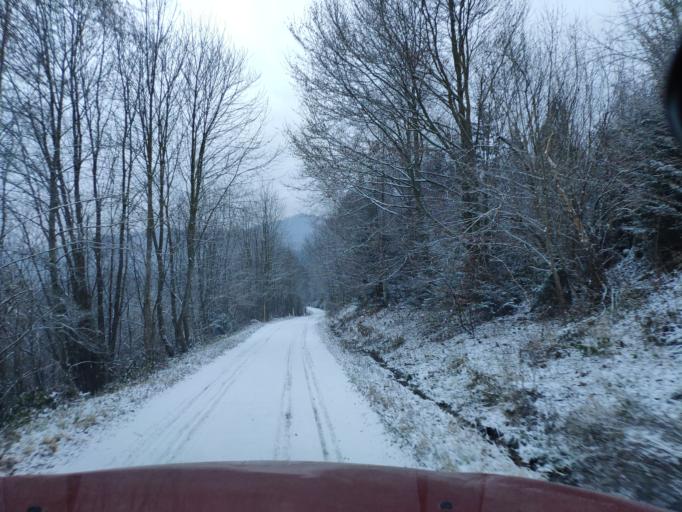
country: SK
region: Kosicky
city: Spisska Nova Ves
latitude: 48.8134
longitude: 20.5554
